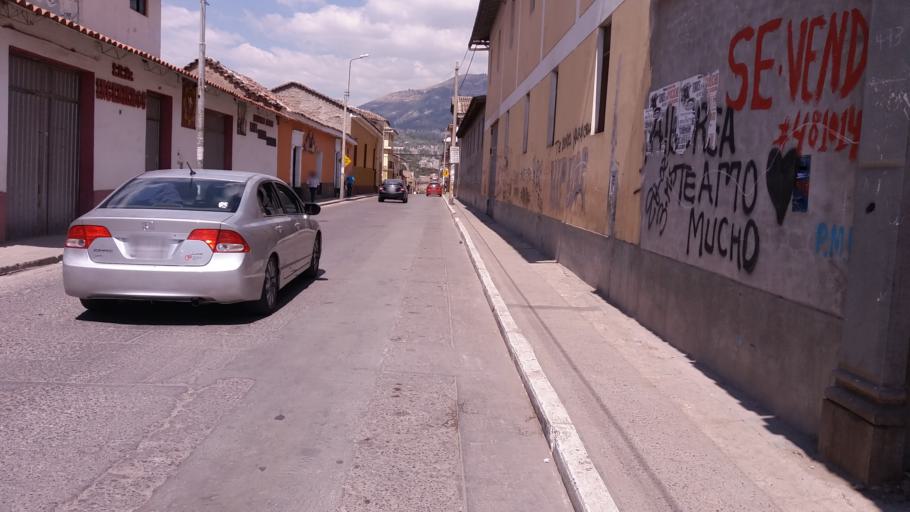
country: PE
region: Ayacucho
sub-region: Provincia de Huamanga
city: Ayacucho
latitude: -13.1594
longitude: -74.2237
